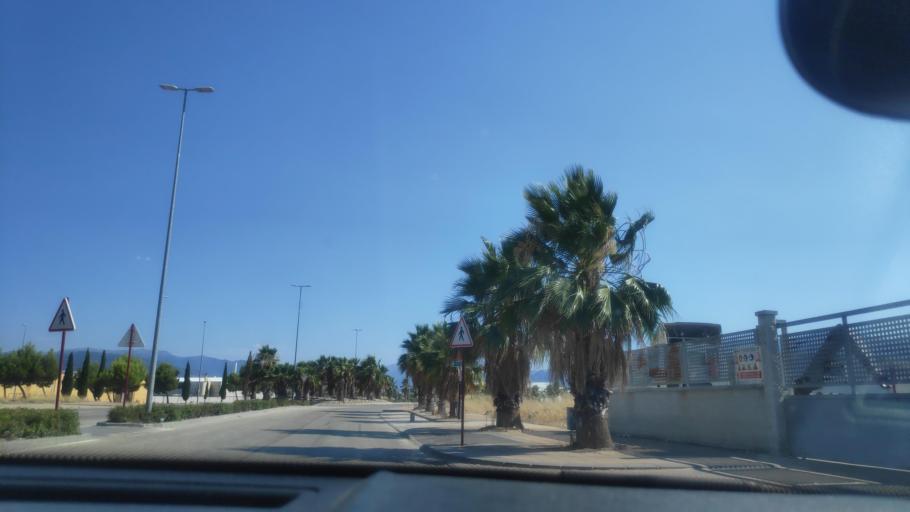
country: ES
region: Andalusia
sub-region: Provincia de Jaen
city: Jaen
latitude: 37.8235
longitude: -3.7759
